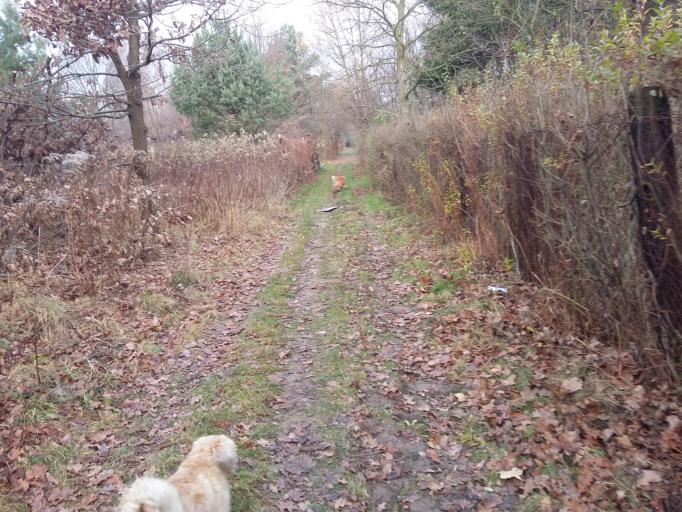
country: PL
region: Lodz Voivodeship
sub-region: Powiat pabianicki
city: Ksawerow
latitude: 51.7329
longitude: 19.4116
